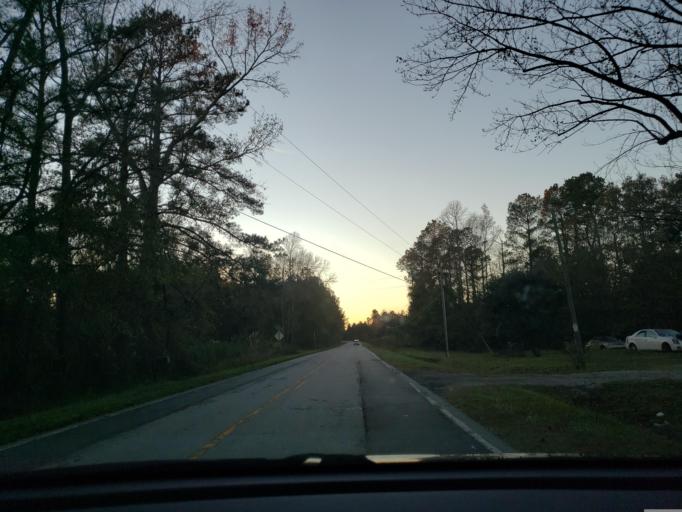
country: US
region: North Carolina
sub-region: Onslow County
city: Half Moon
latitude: 34.7338
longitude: -77.5846
